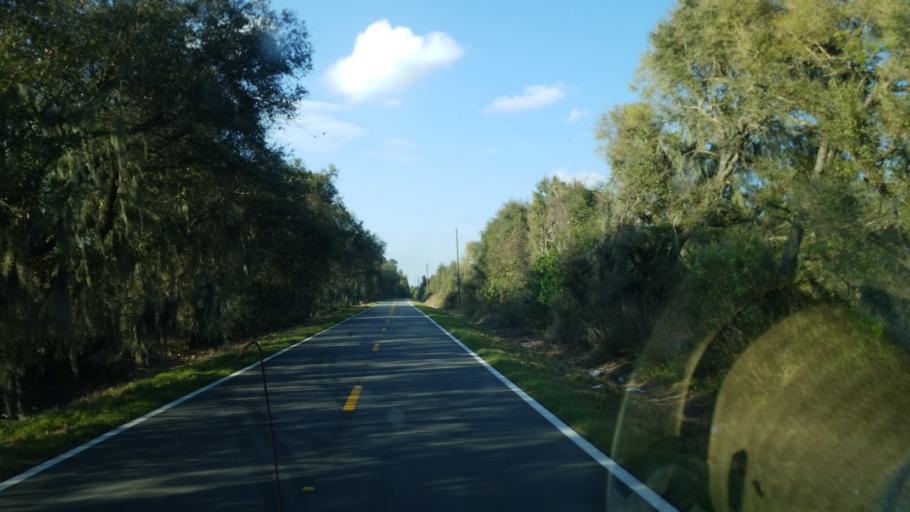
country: US
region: Florida
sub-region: Polk County
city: Mulberry
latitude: 27.7800
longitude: -81.9767
